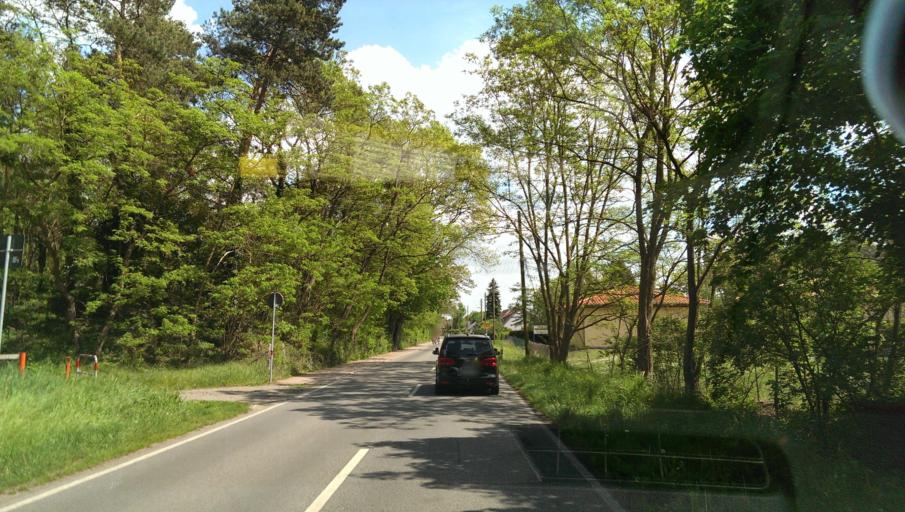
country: DE
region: Saxony-Anhalt
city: Plotzky
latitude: 52.0467
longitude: 11.8168
